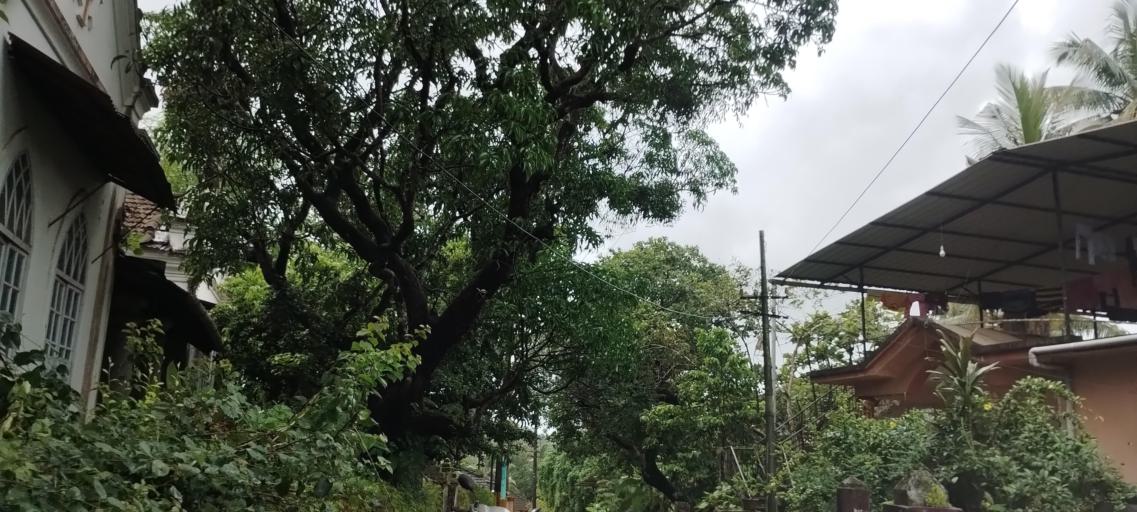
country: IN
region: Goa
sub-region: North Goa
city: Aldona
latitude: 15.5889
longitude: 73.8692
